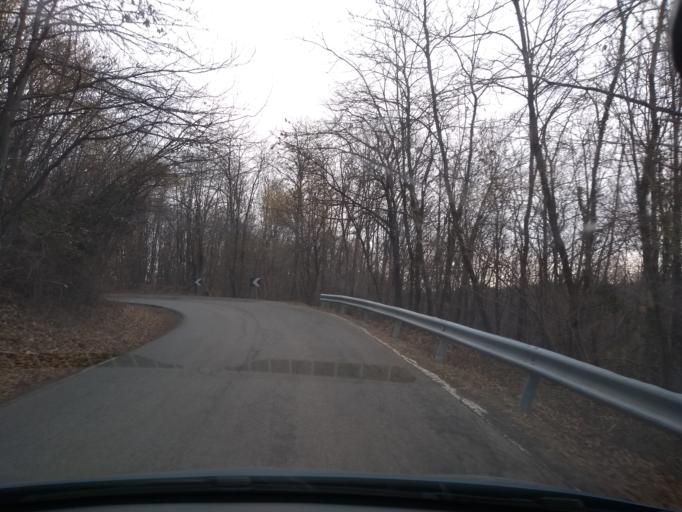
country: IT
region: Piedmont
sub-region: Provincia di Biella
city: Zubiena
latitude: 45.4866
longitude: 7.9813
